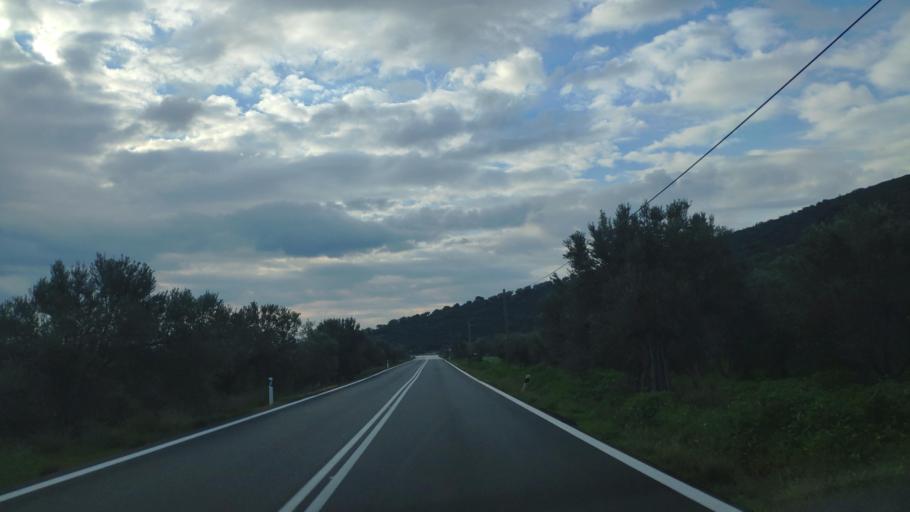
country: GR
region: Peloponnese
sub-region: Nomos Argolidos
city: Koutsopodi
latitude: 37.7433
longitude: 22.7346
